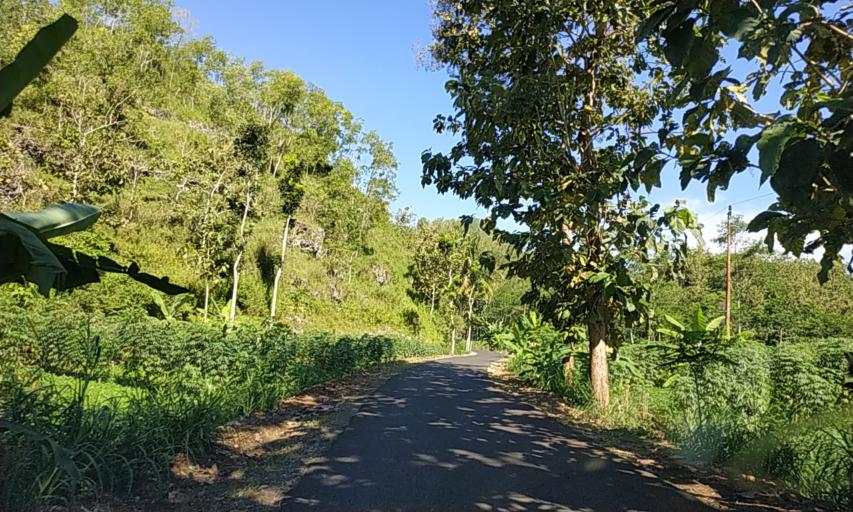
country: ID
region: West Kalimantan
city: Pontianak
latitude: -0.0578
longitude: 109.3484
